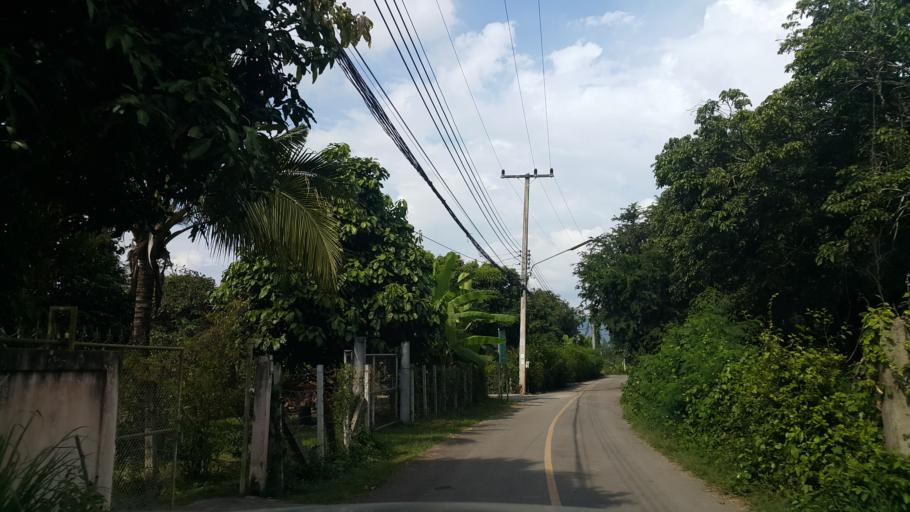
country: TH
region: Chiang Mai
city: San Sai
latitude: 18.9001
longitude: 99.1274
